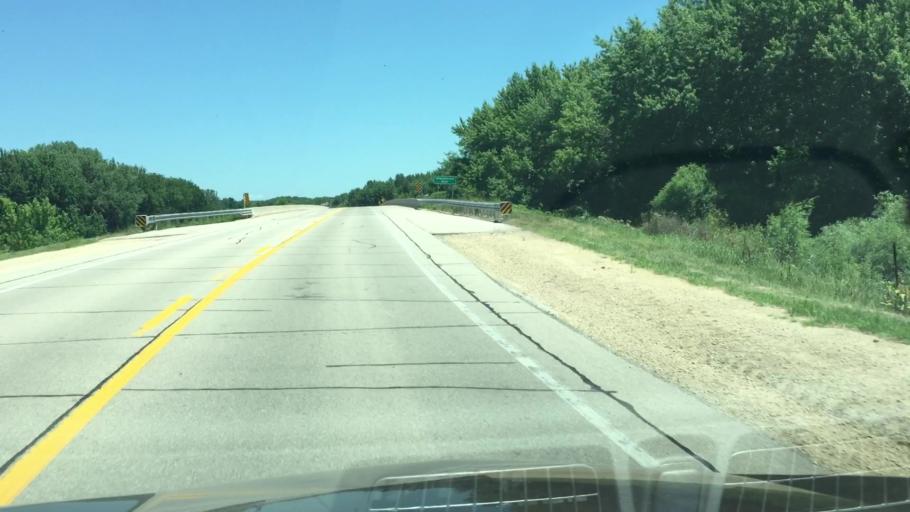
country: US
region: Iowa
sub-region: Cedar County
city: Mechanicsville
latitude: 42.0074
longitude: -91.1409
